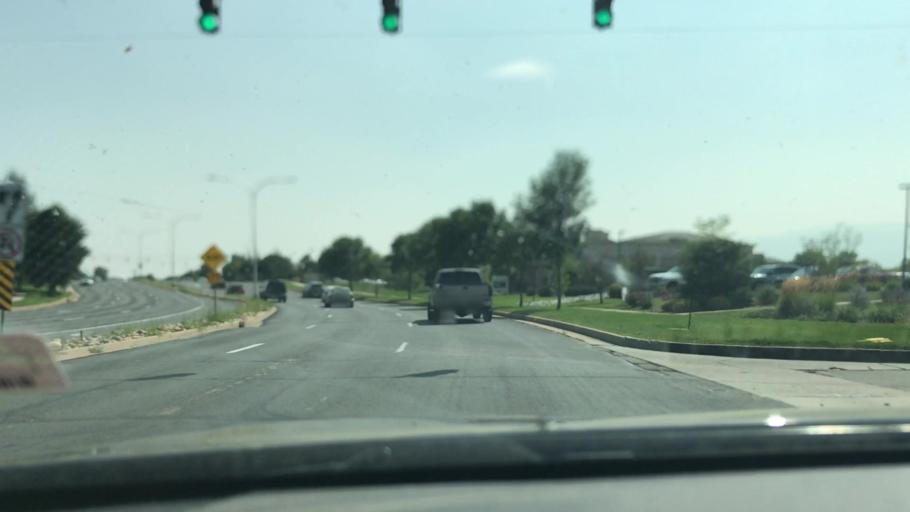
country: US
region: Colorado
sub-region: El Paso County
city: Black Forest
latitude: 38.9593
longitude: -104.7643
